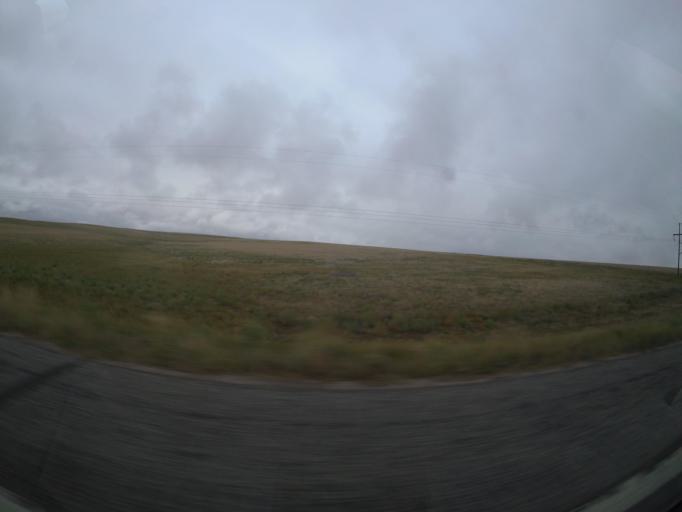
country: US
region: Colorado
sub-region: Washington County
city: Akron
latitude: 39.7397
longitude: -103.4511
